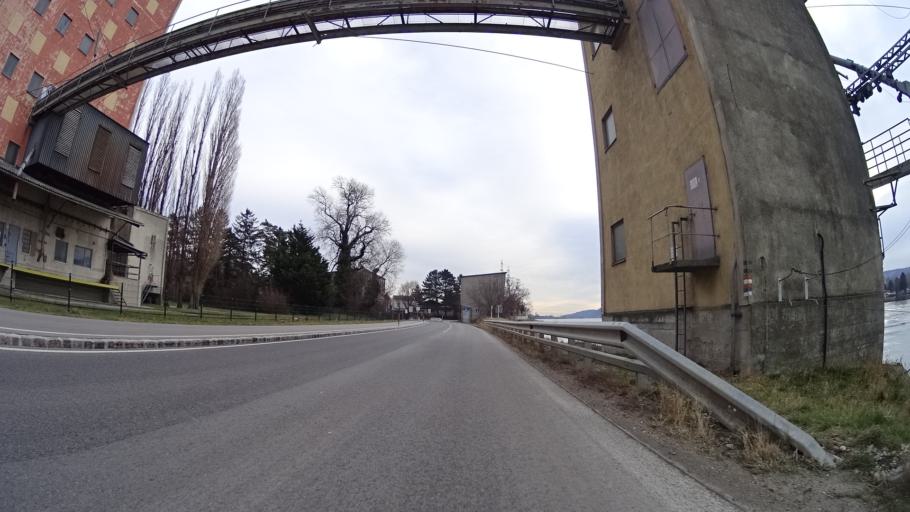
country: AT
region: Lower Austria
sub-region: Politischer Bezirk Korneuburg
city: Bisamberg
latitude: 48.3288
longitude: 16.3333
